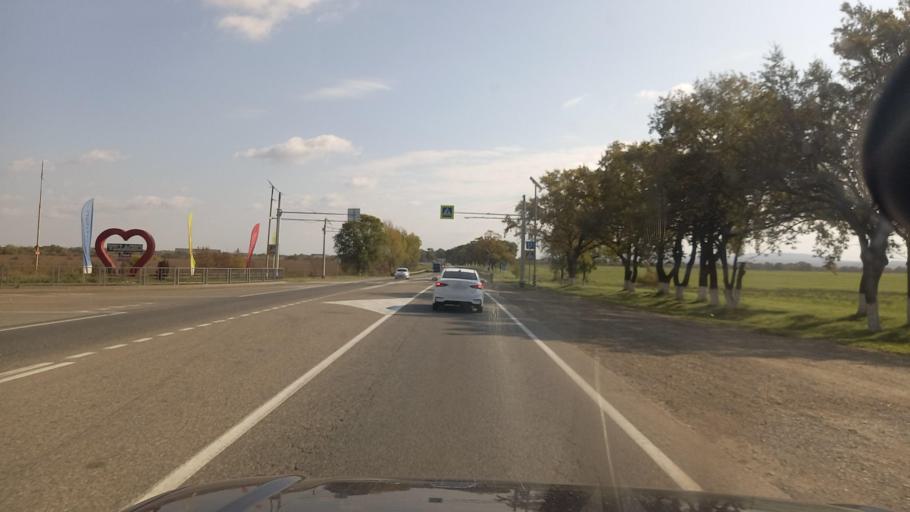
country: RU
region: Krasnodarskiy
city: Akhtyrskiy
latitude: 44.8547
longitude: 38.3336
